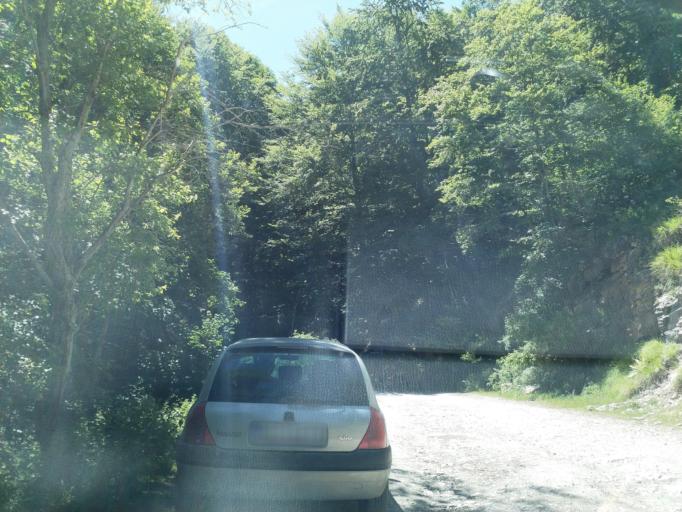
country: XK
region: Mitrovica
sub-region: Komuna e Leposaviqit
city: Leposaviq
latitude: 43.2680
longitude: 20.8569
